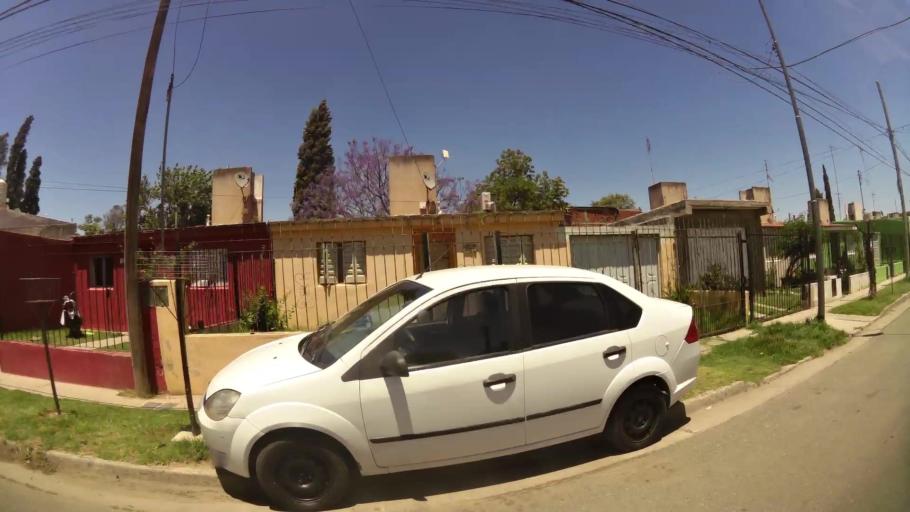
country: AR
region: Cordoba
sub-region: Departamento de Capital
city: Cordoba
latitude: -31.3797
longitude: -64.1300
